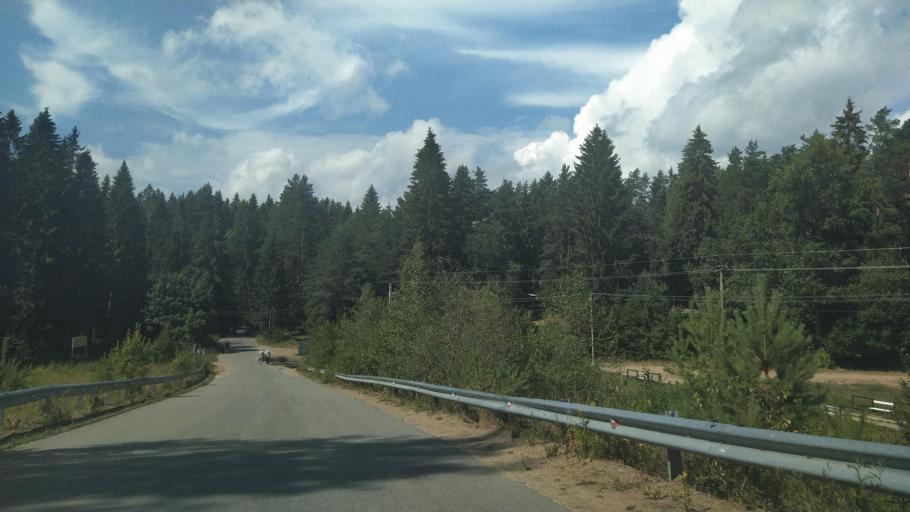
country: RU
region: Leningrad
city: Toksovo
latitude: 60.1677
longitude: 30.5355
